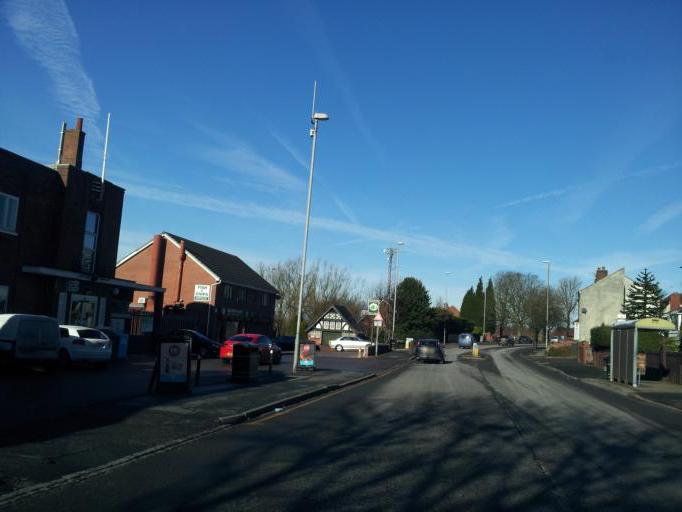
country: GB
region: England
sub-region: Staffordshire
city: Kidsgrove
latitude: 53.0596
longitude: -2.1905
